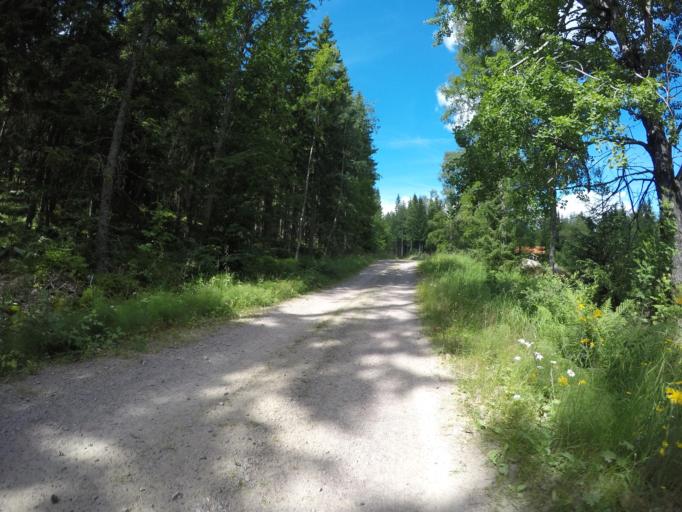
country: SE
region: Vaermland
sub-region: Filipstads Kommun
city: Lesjofors
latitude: 60.0732
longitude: 14.4638
